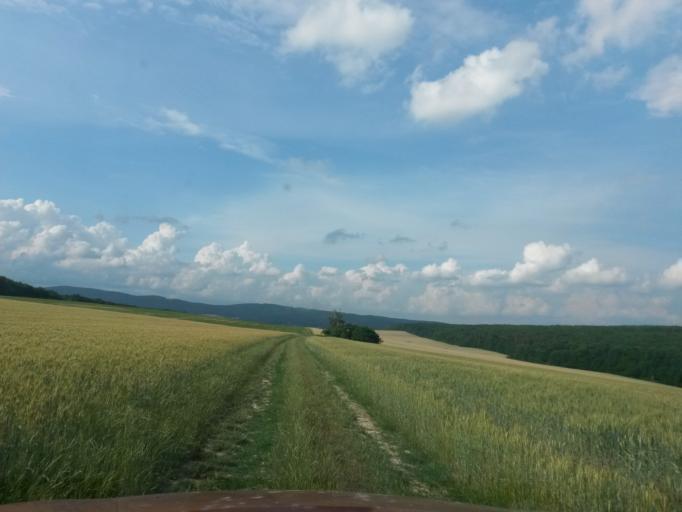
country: SK
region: Kosicky
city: Moldava nad Bodvou
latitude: 48.6318
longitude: 21.1055
